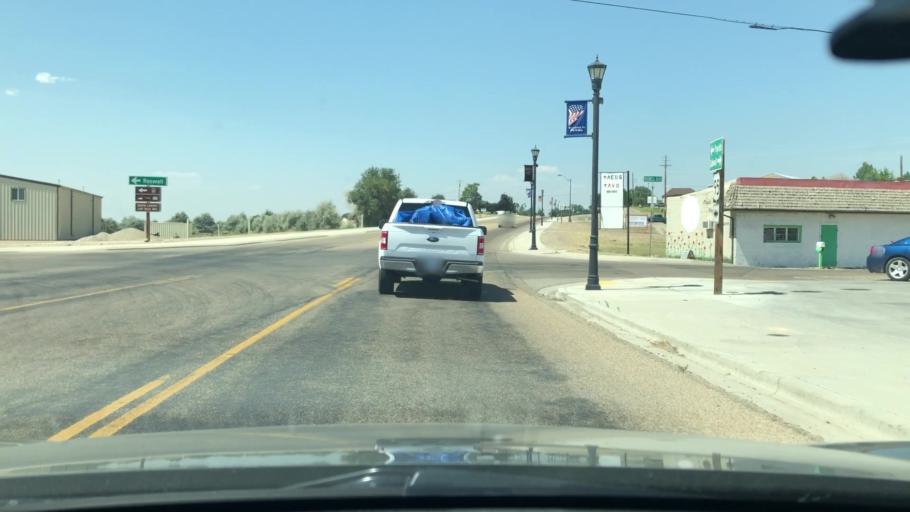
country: US
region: Idaho
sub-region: Canyon County
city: Parma
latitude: 43.7873
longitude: -116.9470
